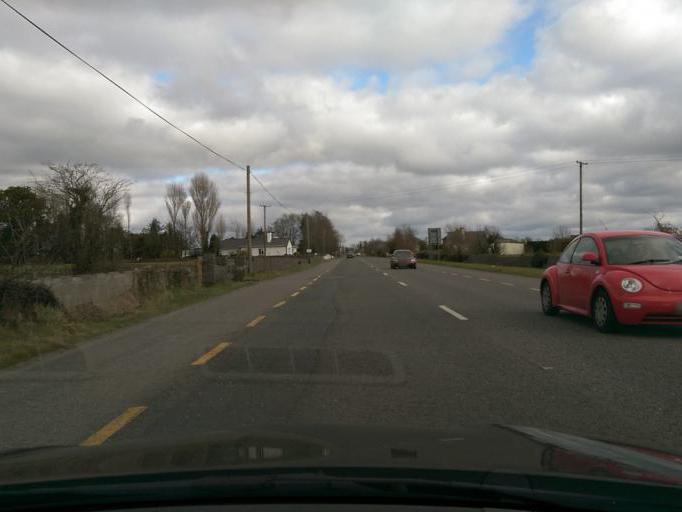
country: IE
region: Connaught
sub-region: County Galway
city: Ballinasloe
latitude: 53.3288
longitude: -8.1824
